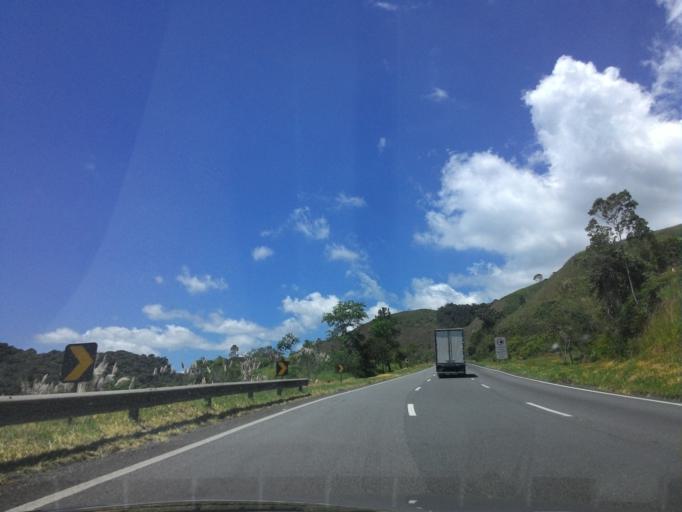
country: BR
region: Sao Paulo
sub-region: Cajati
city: Cajati
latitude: -24.9664
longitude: -48.4603
